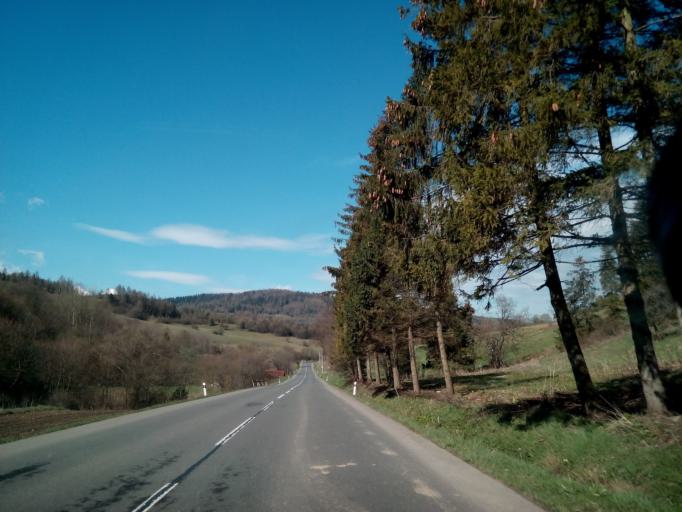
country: SK
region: Presovsky
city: Spisska Bela
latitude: 49.2958
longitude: 20.3951
